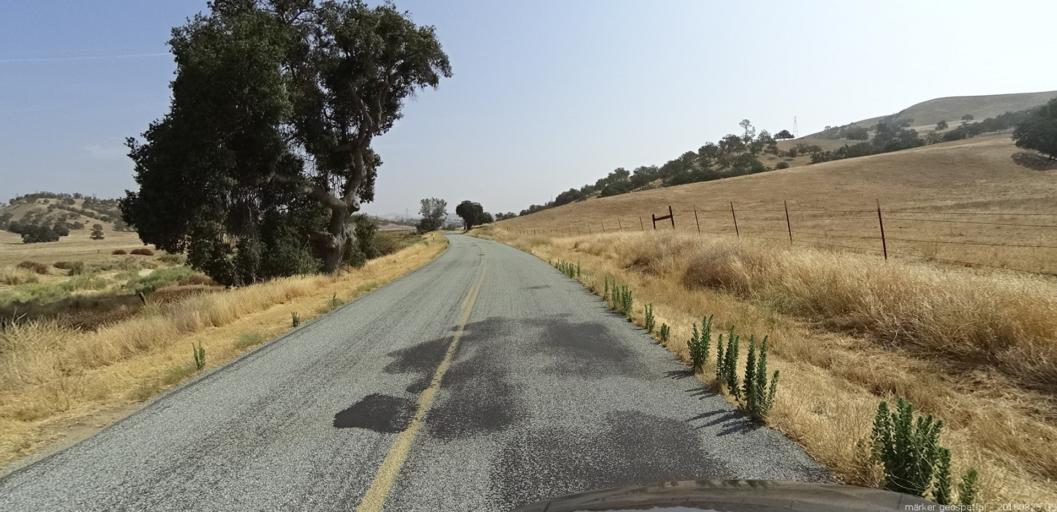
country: US
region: California
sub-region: San Luis Obispo County
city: San Miguel
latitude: 35.8286
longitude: -120.6415
